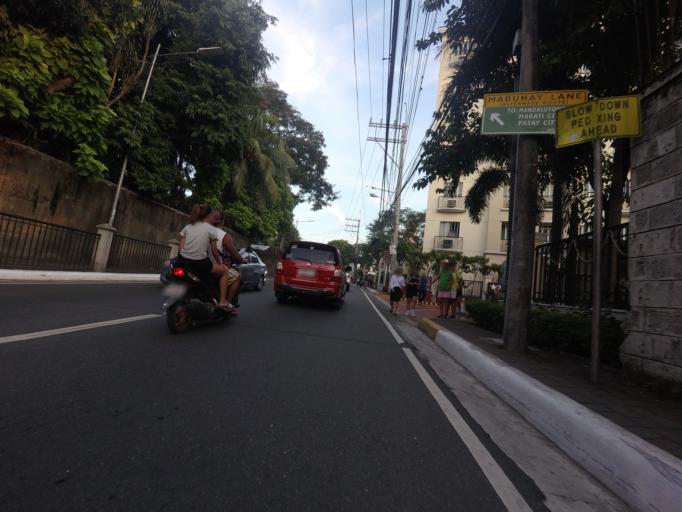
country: PH
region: Metro Manila
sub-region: San Juan
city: San Juan
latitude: 14.6056
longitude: 121.0279
